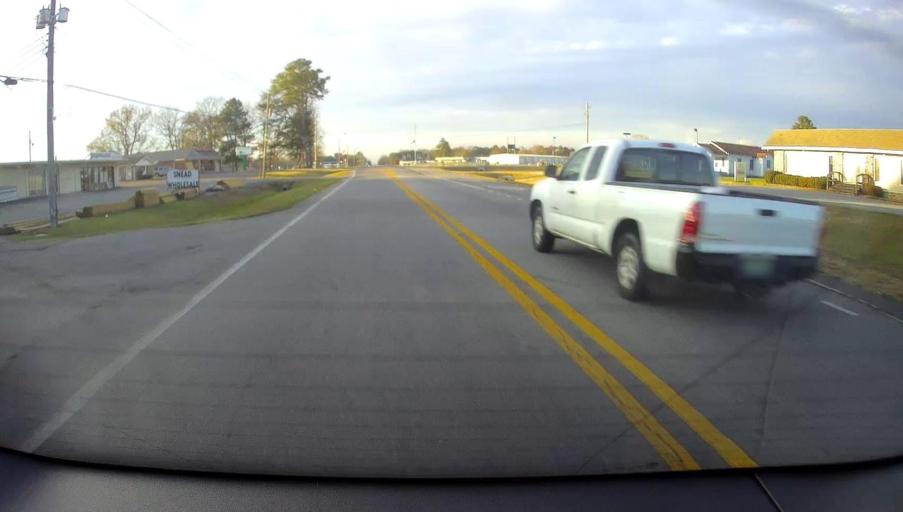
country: US
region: Alabama
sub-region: Blount County
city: Oneonta
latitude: 34.1160
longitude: -86.3895
